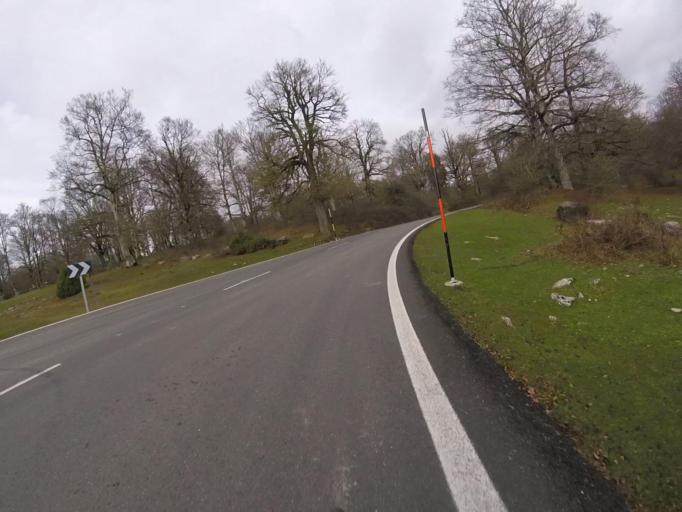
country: ES
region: Navarre
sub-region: Provincia de Navarra
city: Olazagutia
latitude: 42.8388
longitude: -2.1811
